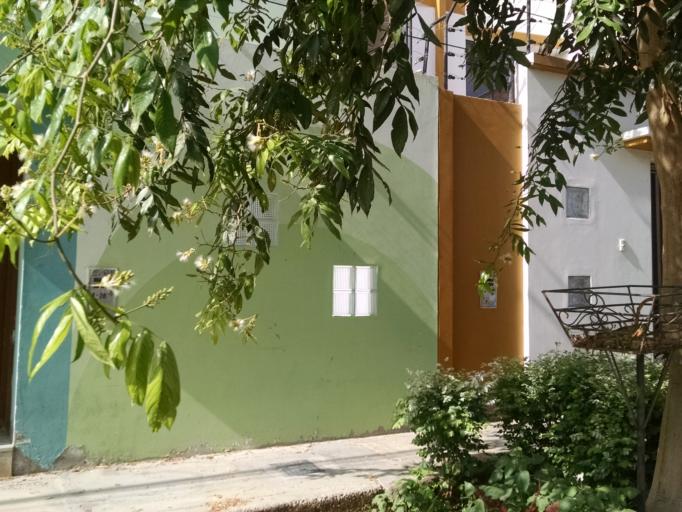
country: PE
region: Piura
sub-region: Provincia de Piura
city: Piura
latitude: -5.1707
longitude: -80.6313
